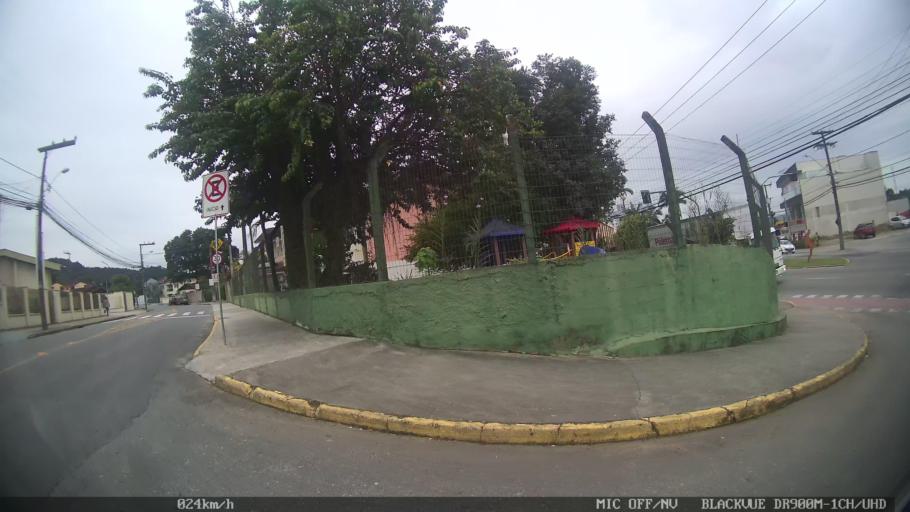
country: BR
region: Santa Catarina
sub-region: Joinville
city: Joinville
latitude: -26.2709
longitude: -48.8267
